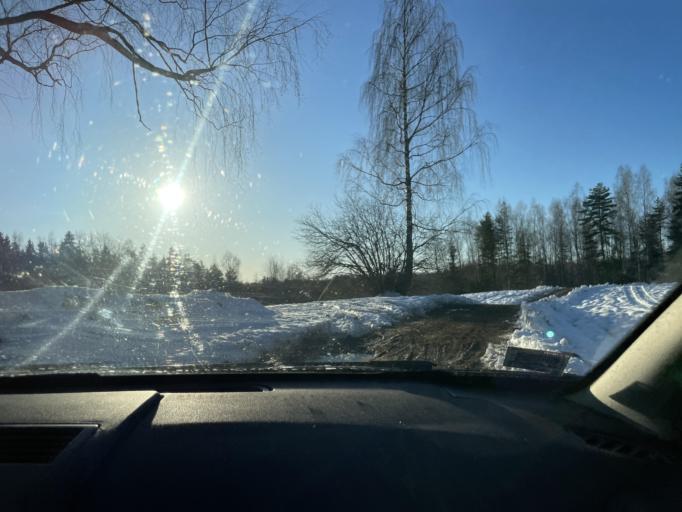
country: LV
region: Ludzas Rajons
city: Ludza
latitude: 56.4482
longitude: 27.6367
